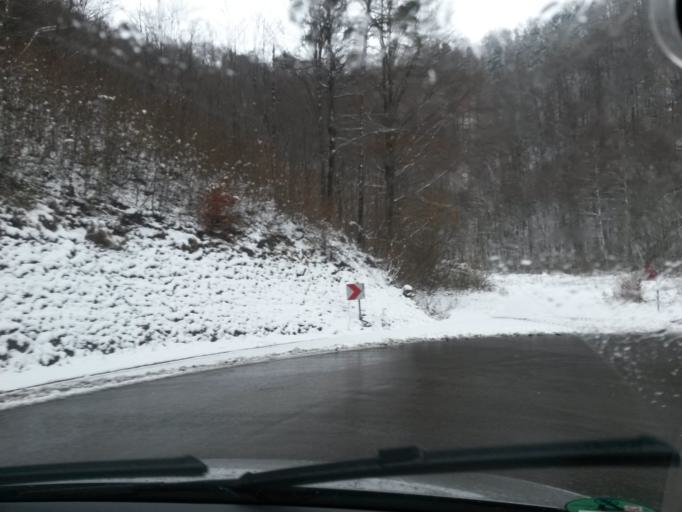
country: DE
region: Baden-Wuerttemberg
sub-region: Regierungsbezirk Stuttgart
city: Deggingen
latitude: 48.5827
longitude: 9.7205
